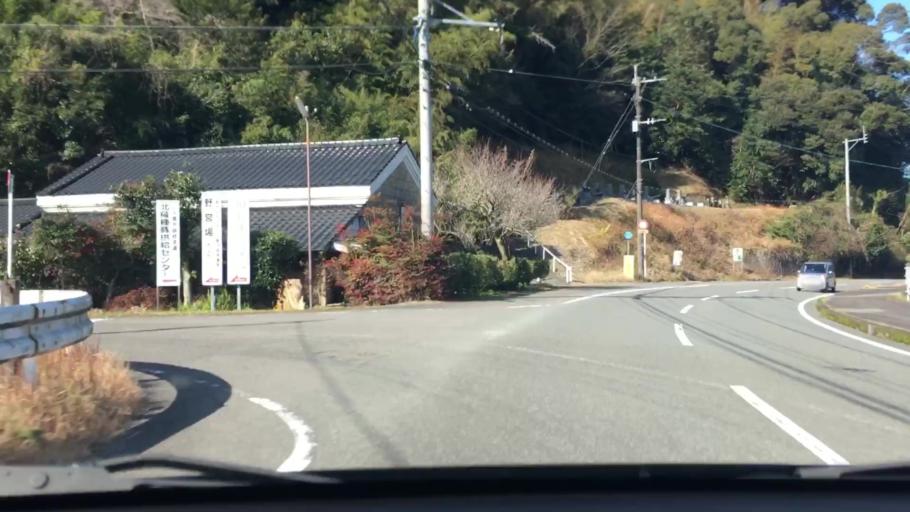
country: JP
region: Kagoshima
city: Ijuin
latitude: 31.7425
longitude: 130.4095
